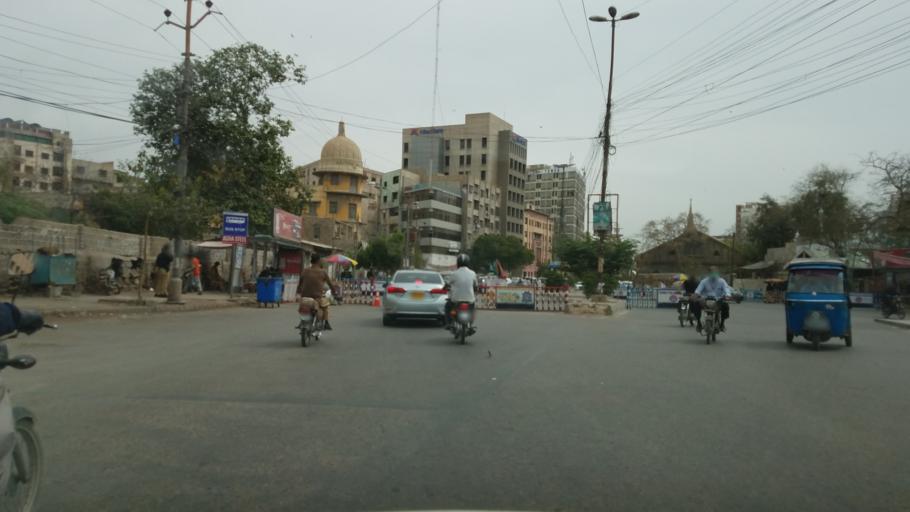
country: PK
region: Sindh
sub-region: Karachi District
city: Karachi
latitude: 24.8478
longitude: 66.9946
